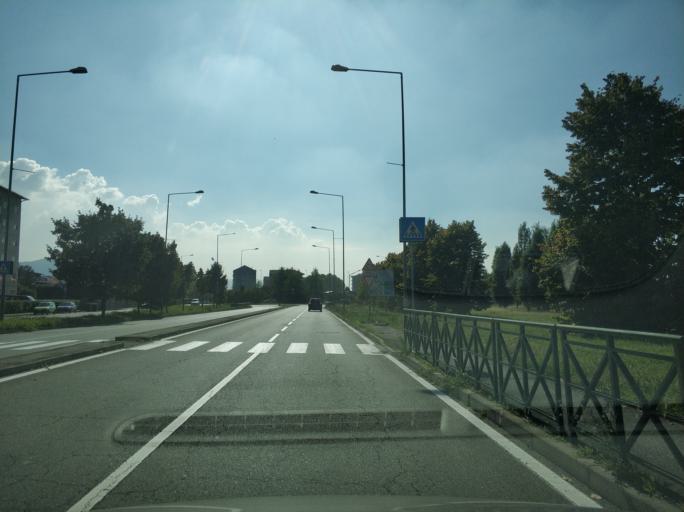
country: IT
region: Piedmont
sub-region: Provincia di Torino
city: Settimo Torinese
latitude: 45.1441
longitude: 7.7580
